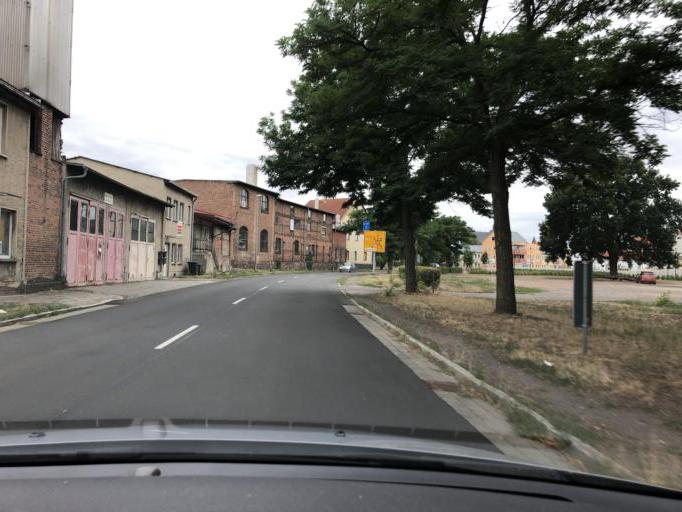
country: DE
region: Saxony-Anhalt
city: Zorbig
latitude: 51.6295
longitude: 12.1247
